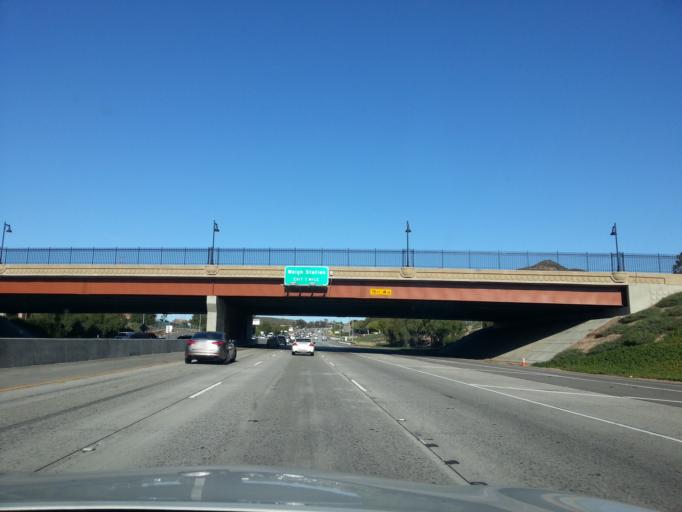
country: US
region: California
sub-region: Ventura County
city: Casa Conejo
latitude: 34.1894
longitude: -118.9384
